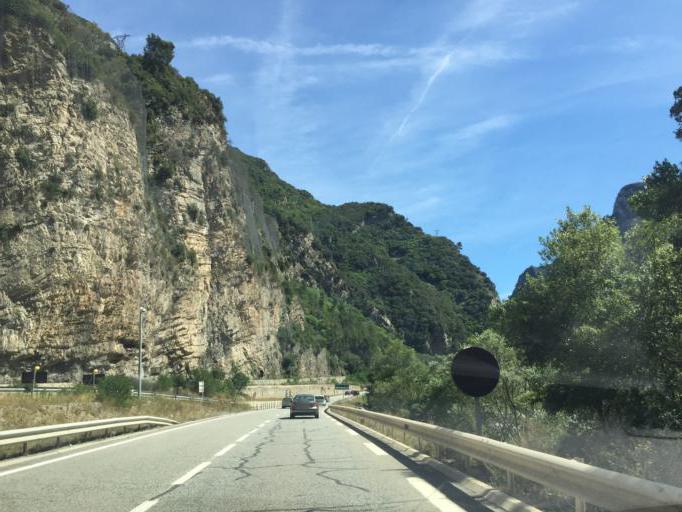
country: FR
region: Provence-Alpes-Cote d'Azur
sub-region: Departement des Alpes-Maritimes
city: Levens
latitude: 43.8873
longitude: 7.1891
